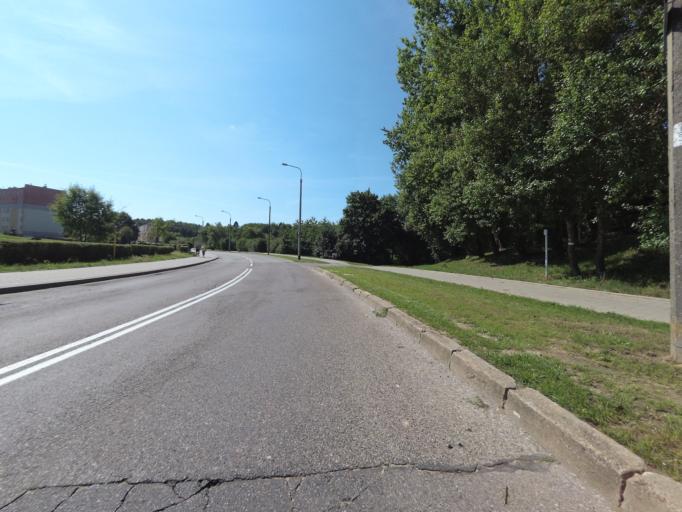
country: PL
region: Pomeranian Voivodeship
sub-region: Gdynia
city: Wielki Kack
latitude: 54.4937
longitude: 18.5076
